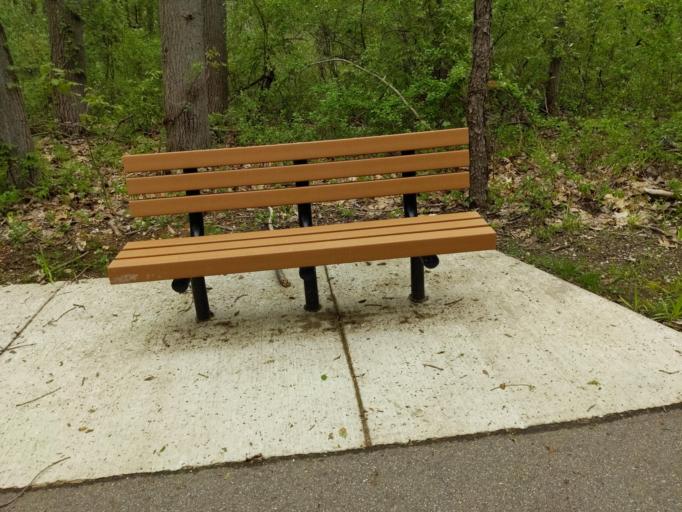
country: US
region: Michigan
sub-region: Washtenaw County
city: Chelsea
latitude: 42.3435
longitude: -84.0392
